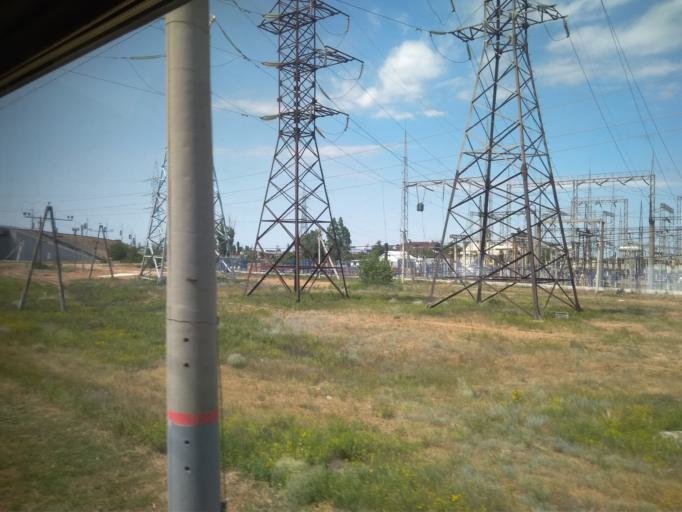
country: RU
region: Volgograd
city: Gumrak
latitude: 48.7607
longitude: 44.4221
